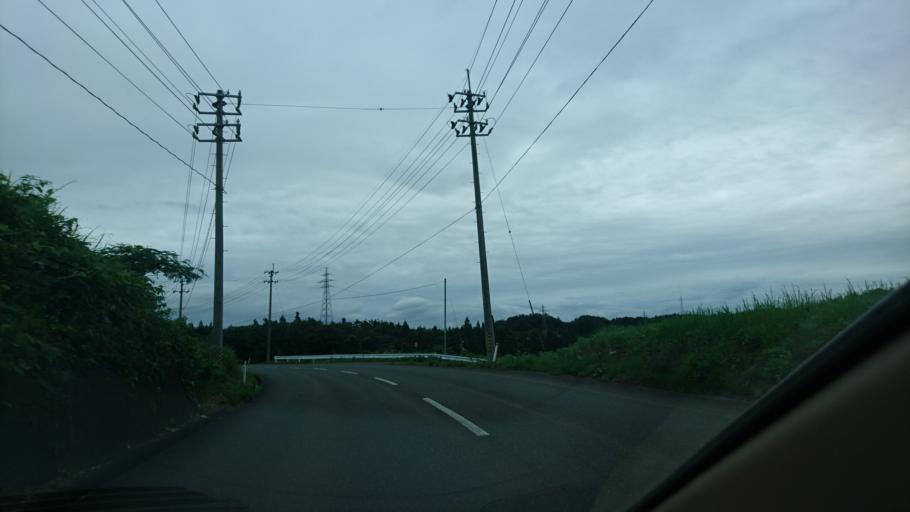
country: JP
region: Iwate
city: Mizusawa
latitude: 39.1967
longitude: 141.1956
